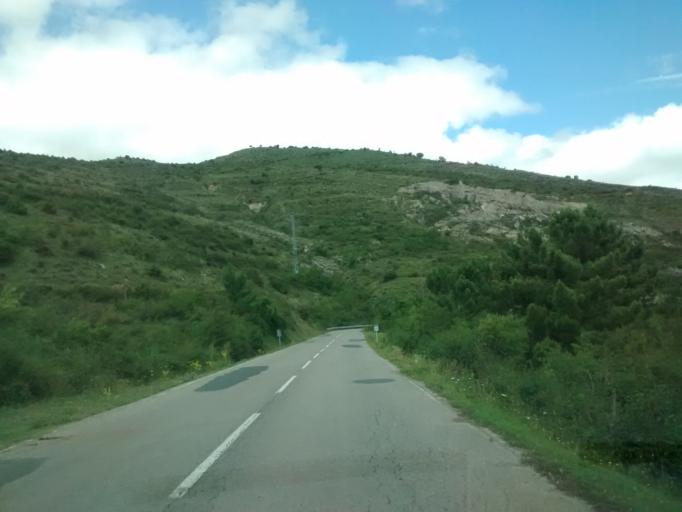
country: ES
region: La Rioja
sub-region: Provincia de La Rioja
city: Soto en Cameros
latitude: 42.2740
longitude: -2.4326
